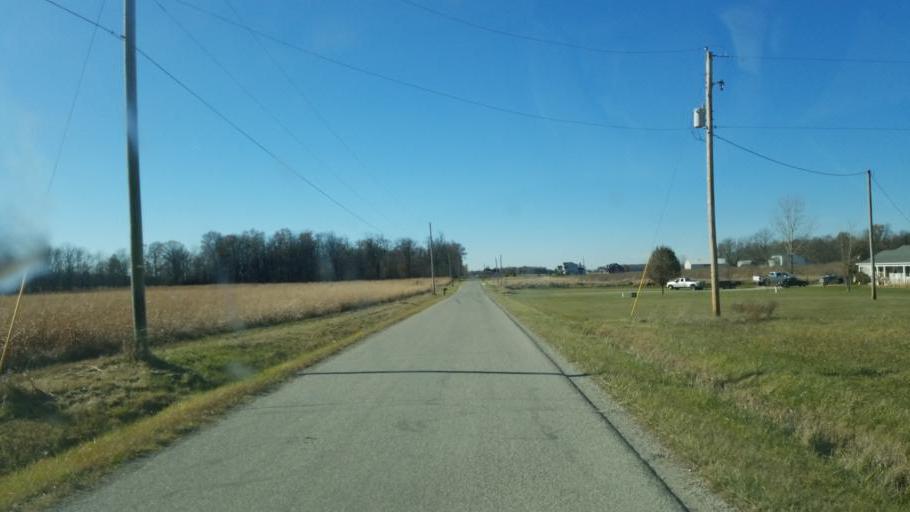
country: US
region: Ohio
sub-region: Crawford County
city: Galion
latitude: 40.7706
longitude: -82.8397
